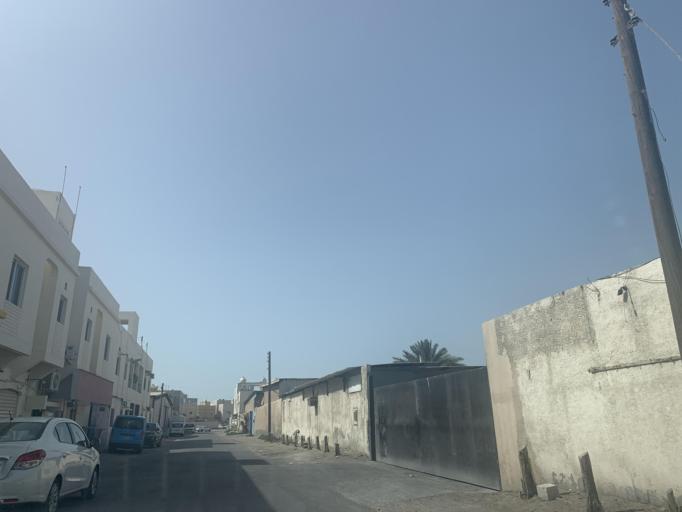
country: BH
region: Northern
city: Sitrah
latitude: 26.1670
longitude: 50.6160
